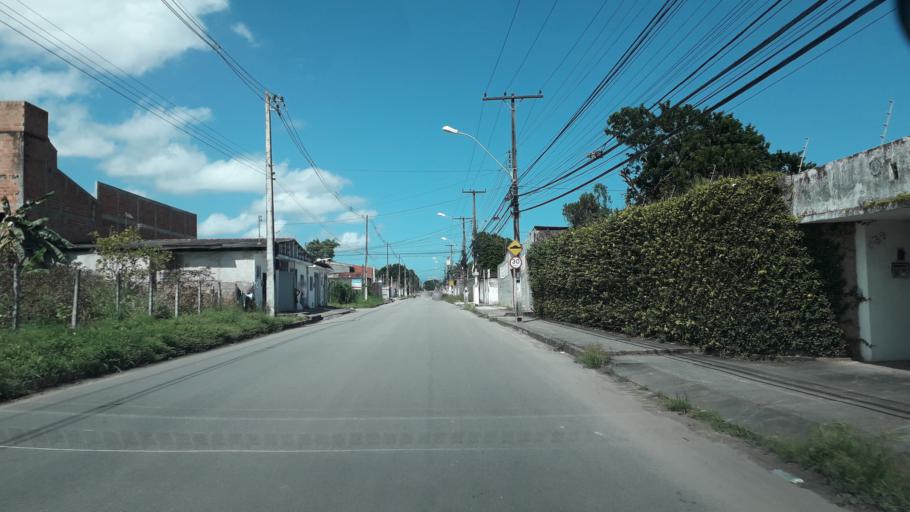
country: BR
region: Alagoas
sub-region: Satuba
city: Satuba
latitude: -9.5560
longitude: -35.7847
